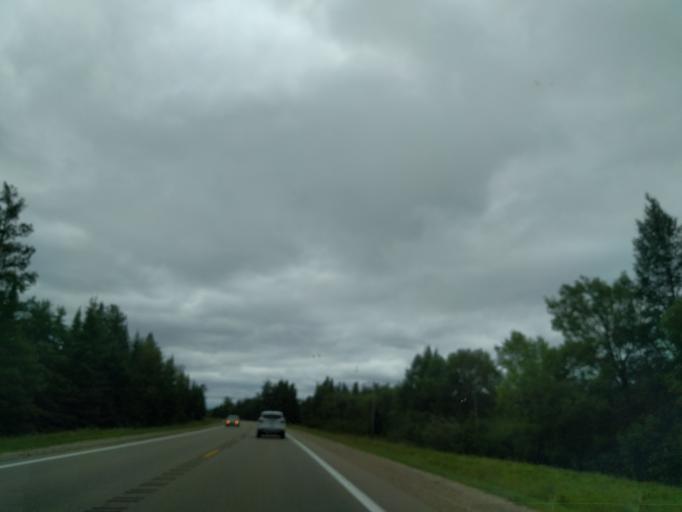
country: US
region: Michigan
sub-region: Delta County
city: Escanaba
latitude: 45.5217
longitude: -87.2886
